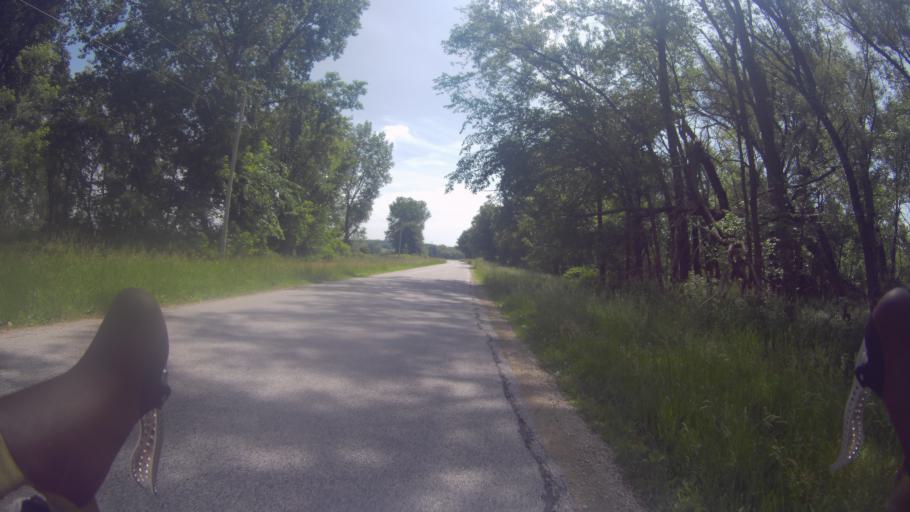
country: US
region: Wisconsin
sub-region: Jefferson County
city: Cambridge
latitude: 43.0548
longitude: -89.0143
